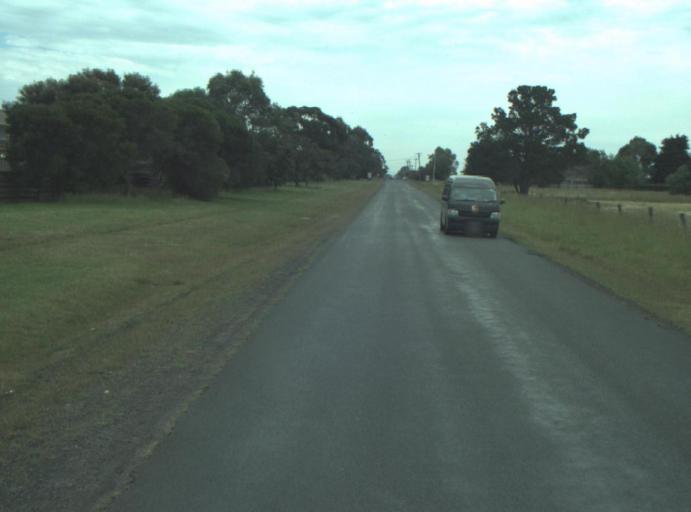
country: AU
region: Victoria
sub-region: Greater Geelong
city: Breakwater
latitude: -38.1890
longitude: 144.3997
